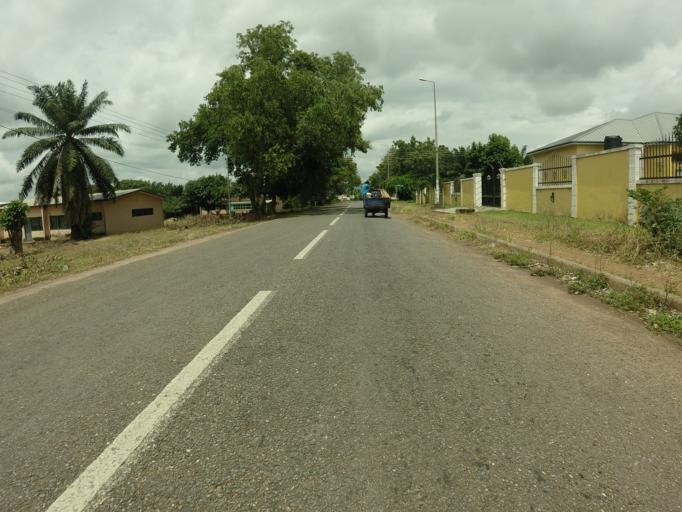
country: GH
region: Volta
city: Ho
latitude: 6.5963
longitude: 0.4801
